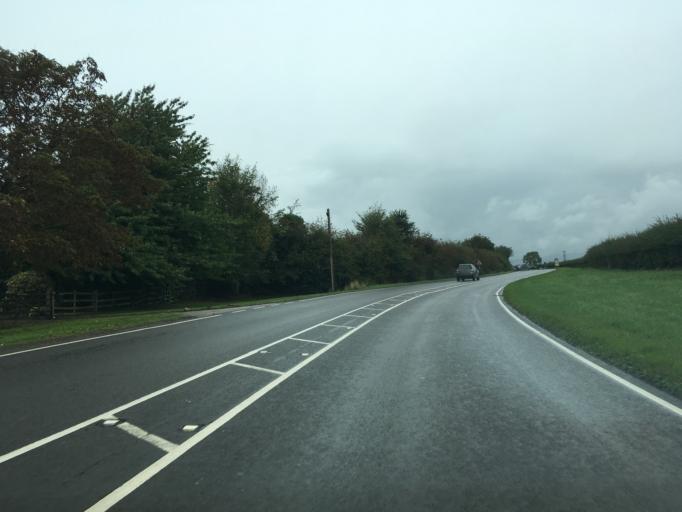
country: GB
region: England
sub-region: Nottinghamshire
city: Ruddington
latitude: 52.8712
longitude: -1.1310
